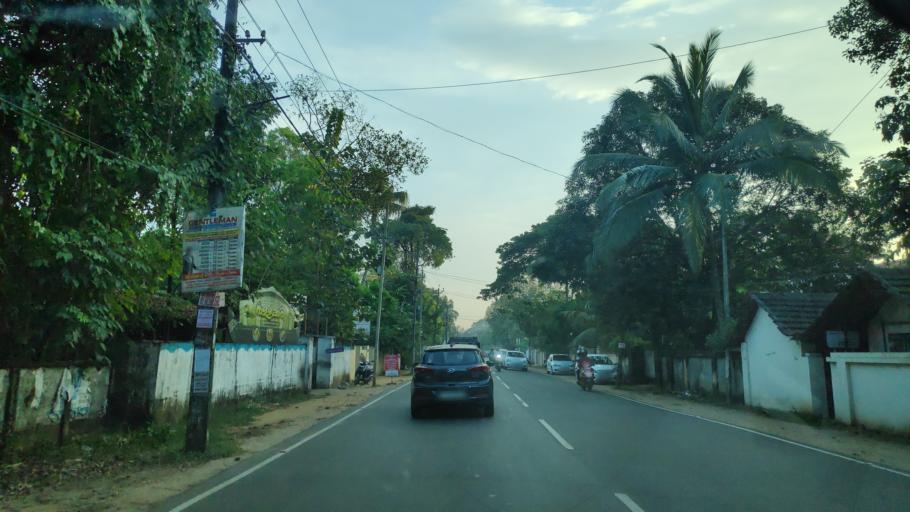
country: IN
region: Kerala
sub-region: Alappuzha
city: Shertallai
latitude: 9.6786
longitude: 76.3410
